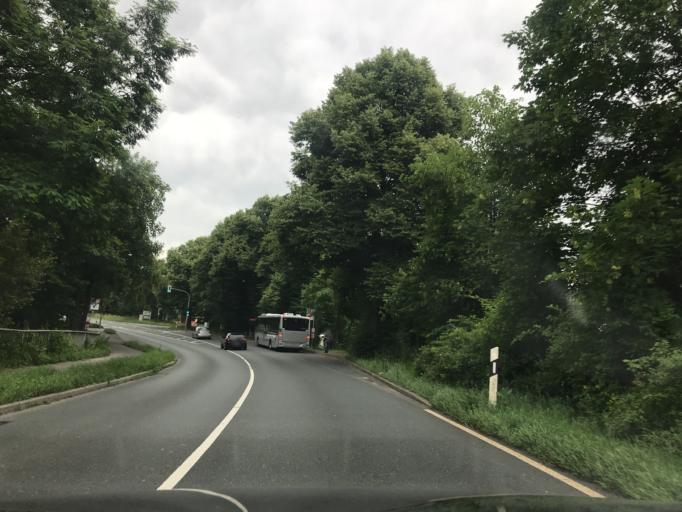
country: DE
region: North Rhine-Westphalia
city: Haan
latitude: 51.1965
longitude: 6.9714
